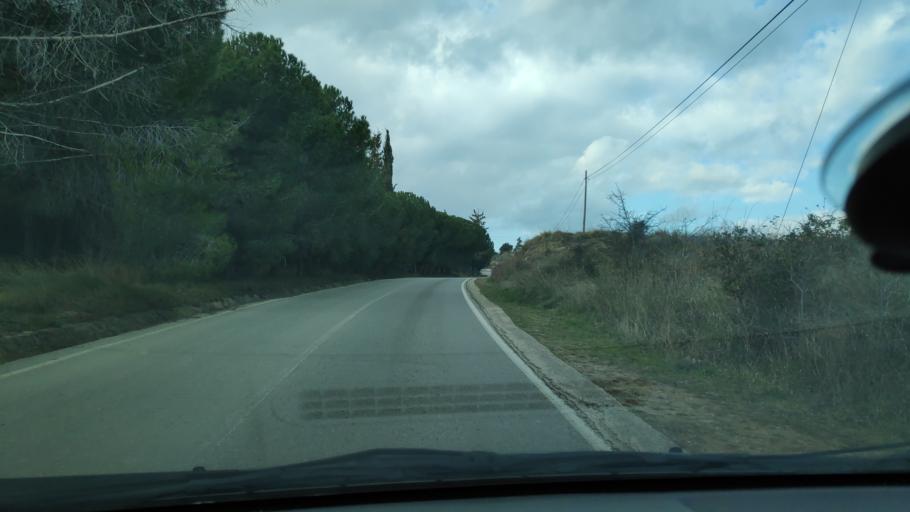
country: ES
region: Catalonia
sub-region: Provincia de Barcelona
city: Terrassa
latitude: 41.5687
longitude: 1.9927
